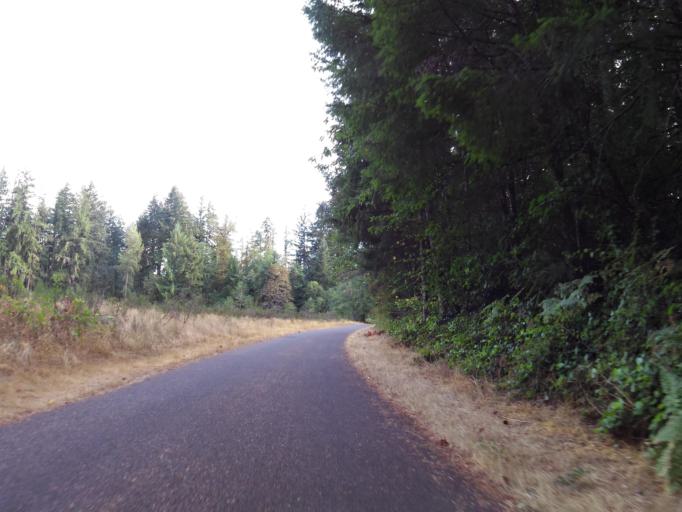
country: US
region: Washington
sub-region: Thurston County
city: Lacey
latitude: 46.9610
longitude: -122.8117
